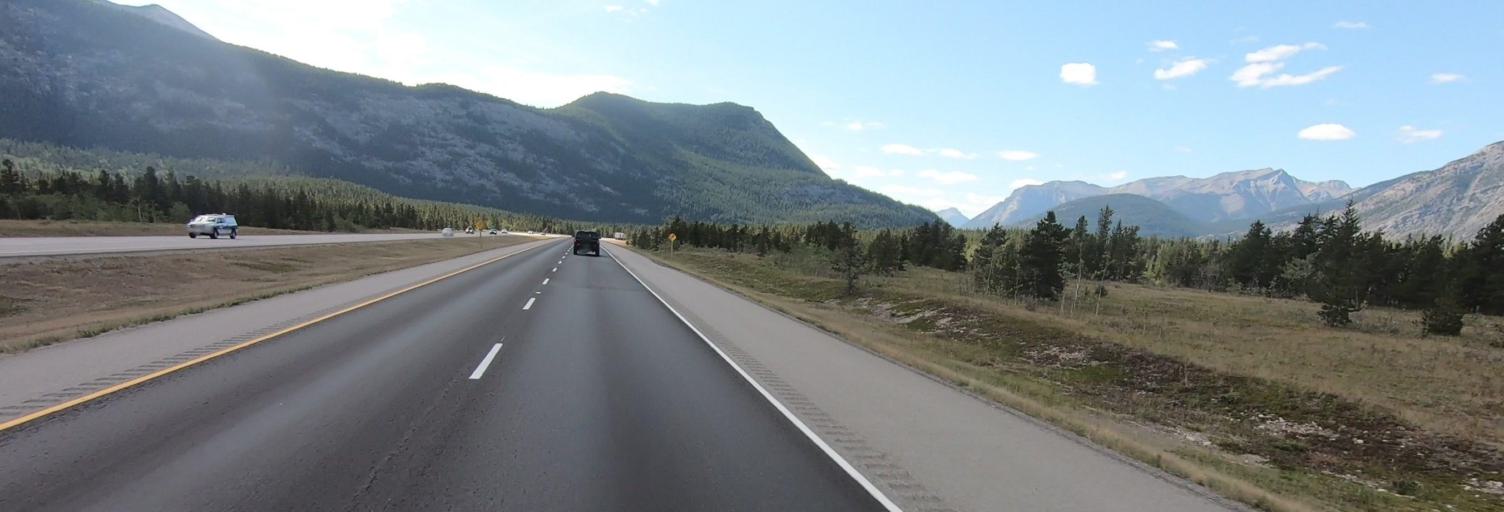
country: CA
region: Alberta
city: Canmore
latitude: 51.0698
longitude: -115.0816
